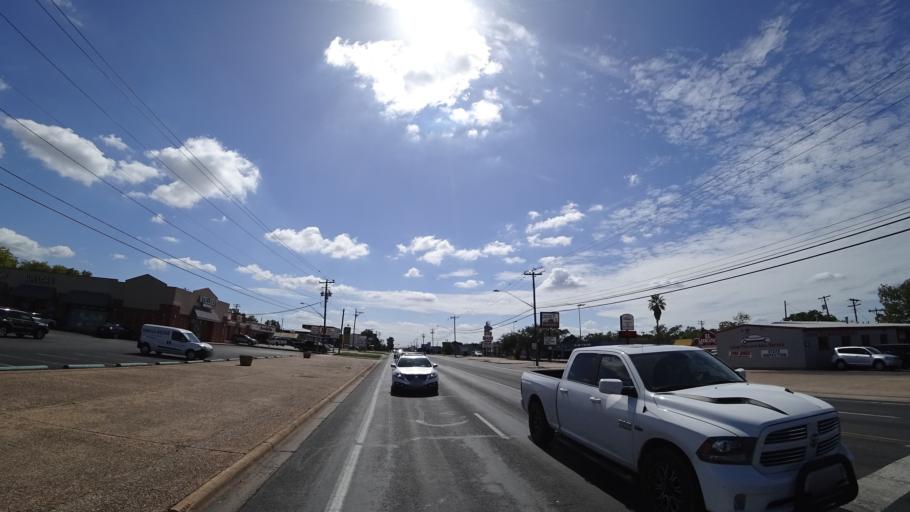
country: US
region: Texas
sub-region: Travis County
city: Austin
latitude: 30.3504
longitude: -97.7343
